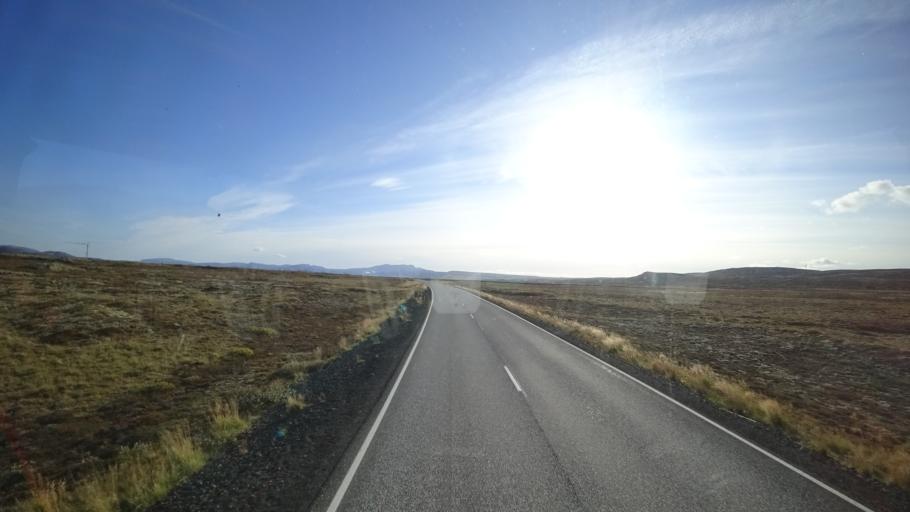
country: IS
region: South
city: Hveragerdi
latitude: 64.2614
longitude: -21.1347
